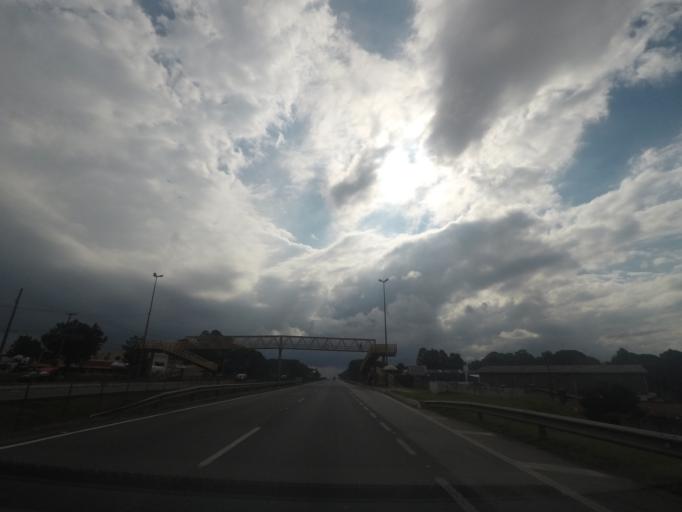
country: BR
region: Parana
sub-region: Sao Jose Dos Pinhais
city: Sao Jose dos Pinhais
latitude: -25.5085
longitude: -49.1346
